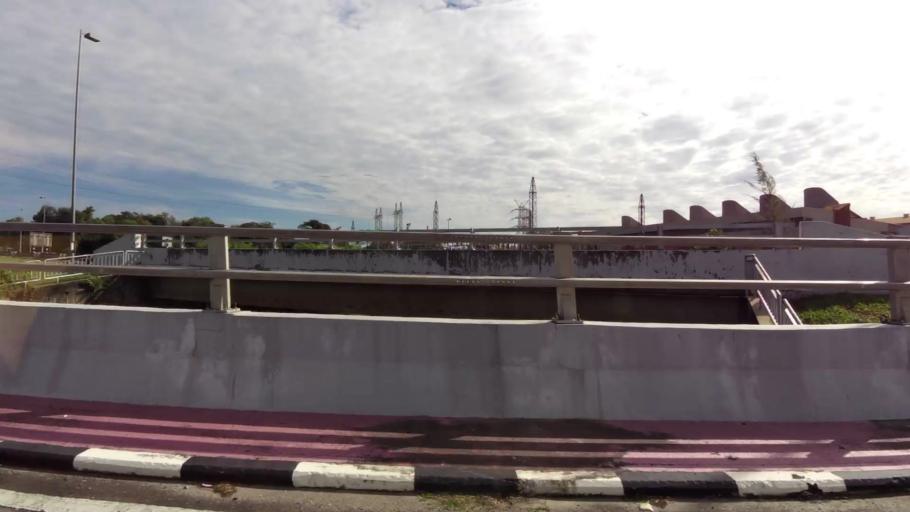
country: BN
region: Brunei and Muara
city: Bandar Seri Begawan
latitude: 4.9076
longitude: 114.9095
